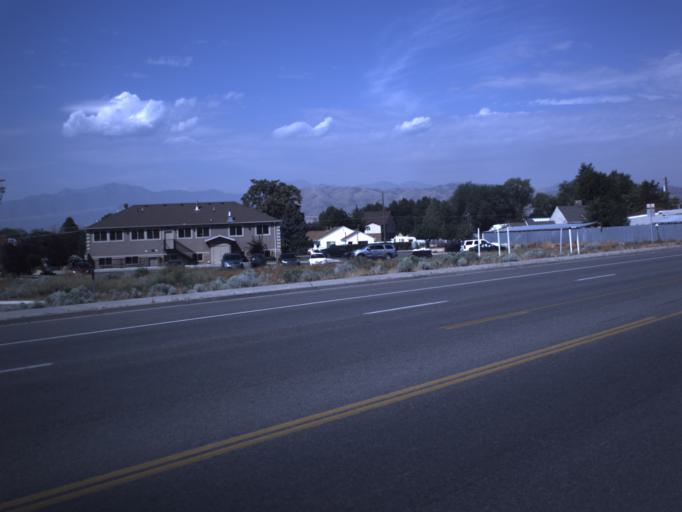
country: US
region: Utah
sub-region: Utah County
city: Lehi
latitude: 40.4024
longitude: -111.8553
